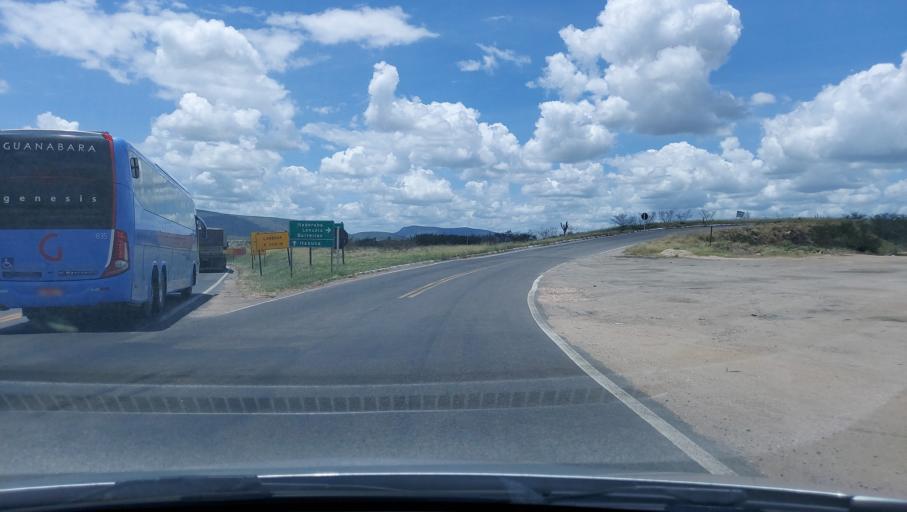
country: BR
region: Bahia
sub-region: Castro Alves
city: Castro Alves
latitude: -12.5829
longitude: -39.5207
